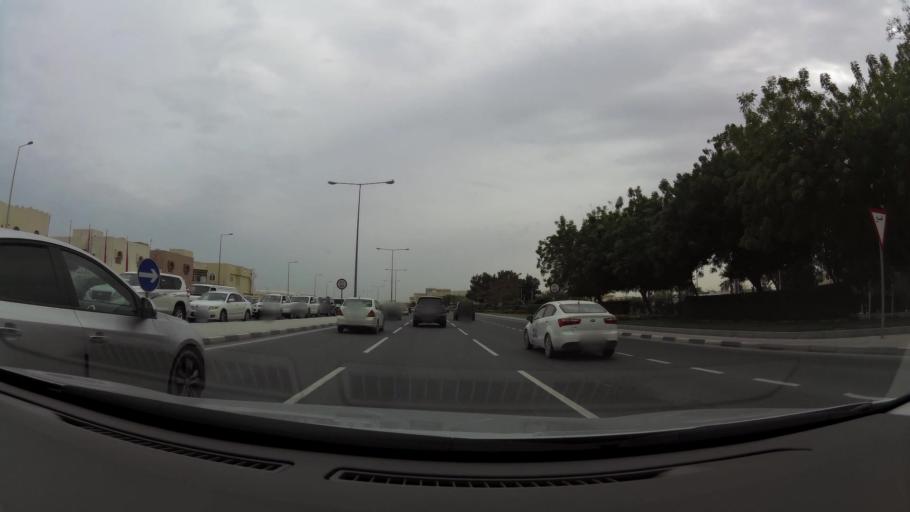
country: QA
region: Baladiyat ad Dawhah
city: Doha
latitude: 25.3341
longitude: 51.4819
